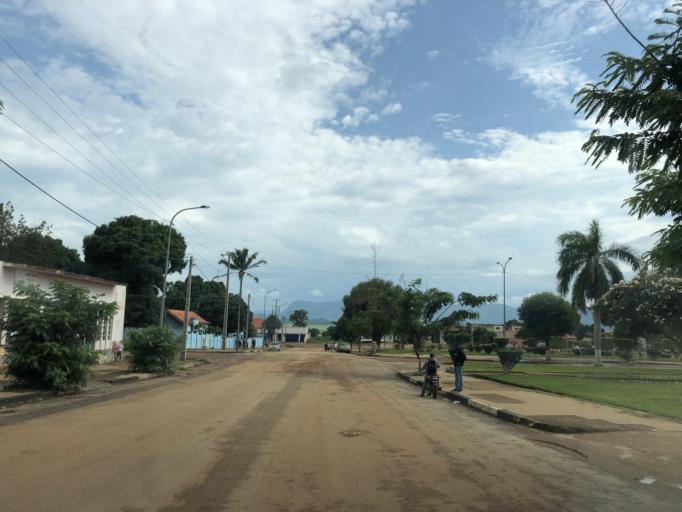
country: AO
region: Cuanza Sul
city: Uacu Cungo
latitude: -11.3633
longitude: 15.1182
